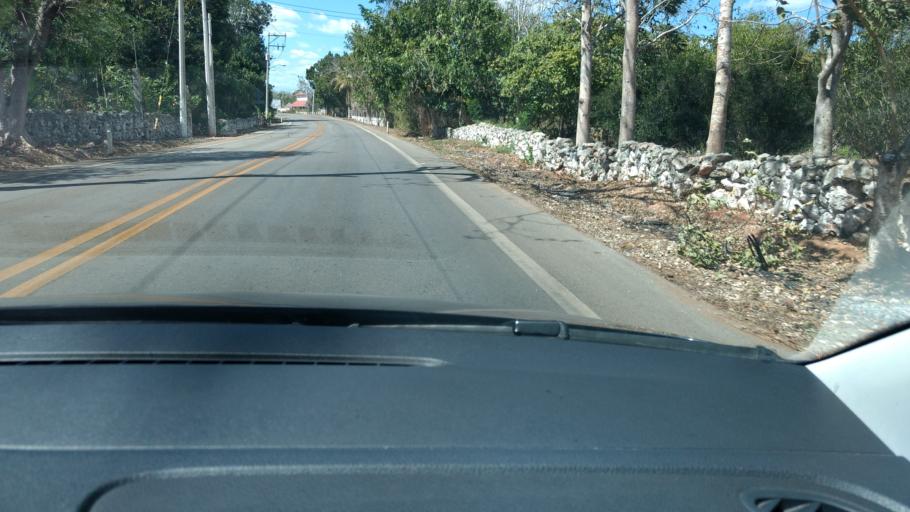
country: MX
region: Yucatan
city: Tzucacab
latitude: 20.0796
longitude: -89.0639
